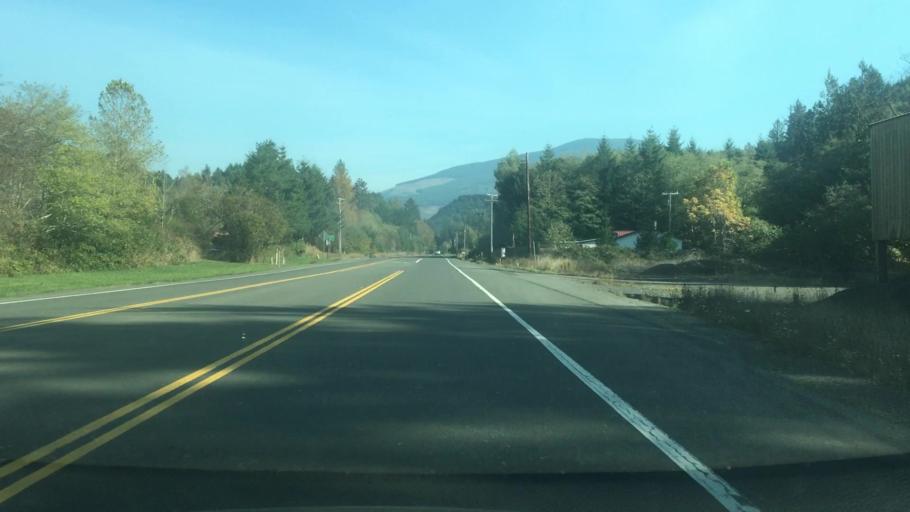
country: US
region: Oregon
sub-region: Lincoln County
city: Rose Lodge
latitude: 45.0213
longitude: -123.8598
